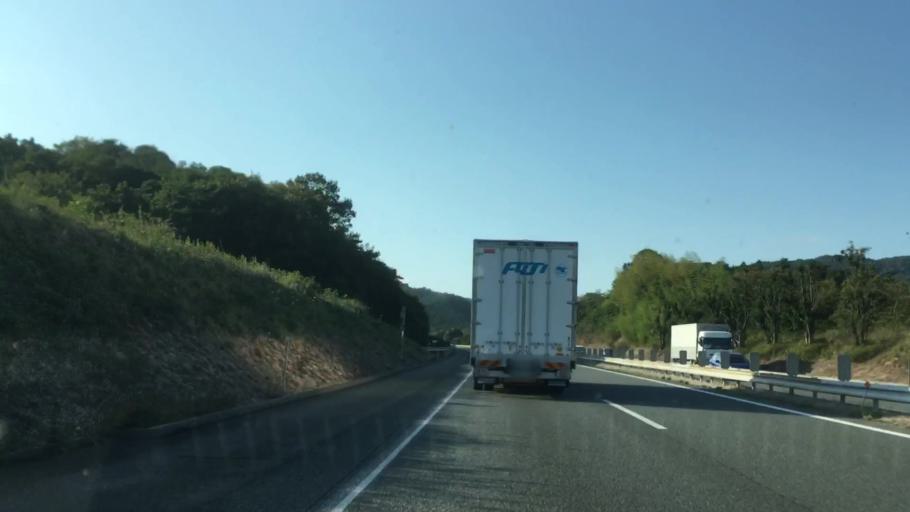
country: JP
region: Yamaguchi
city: Hofu
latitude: 34.0739
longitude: 131.4943
